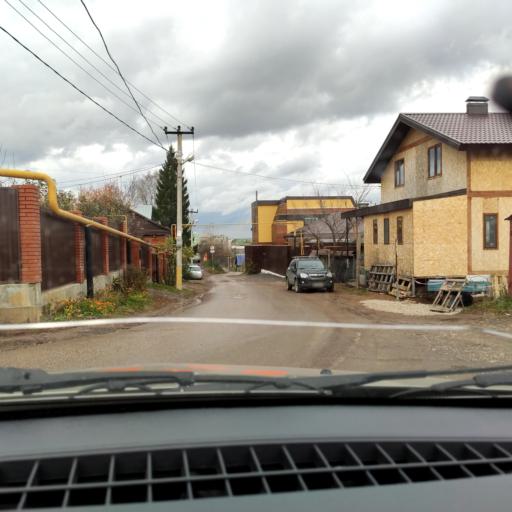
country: RU
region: Bashkortostan
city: Ufa
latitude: 54.7556
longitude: 56.0419
